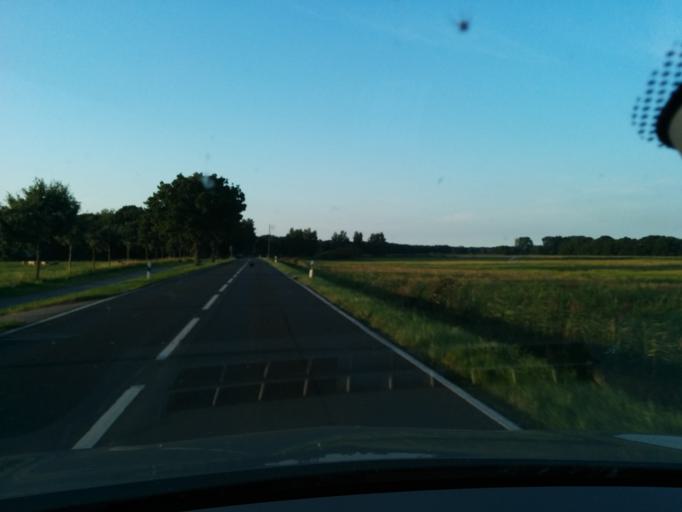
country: DE
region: Mecklenburg-Vorpommern
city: Seebad Bansin
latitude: 53.9750
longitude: 14.0738
